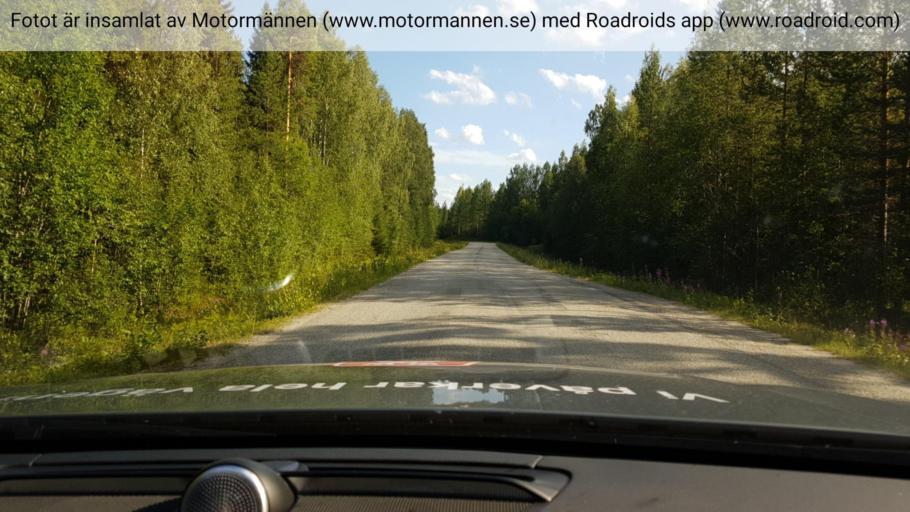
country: SE
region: Vaesterbotten
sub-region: Dorotea Kommun
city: Dorotea
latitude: 63.9133
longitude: 16.2683
